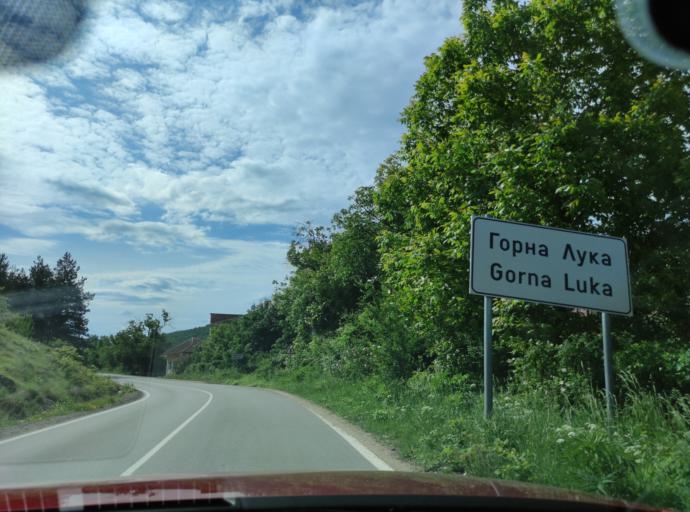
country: BG
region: Montana
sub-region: Obshtina Chiprovtsi
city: Chiprovtsi
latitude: 43.4536
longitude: 22.9050
